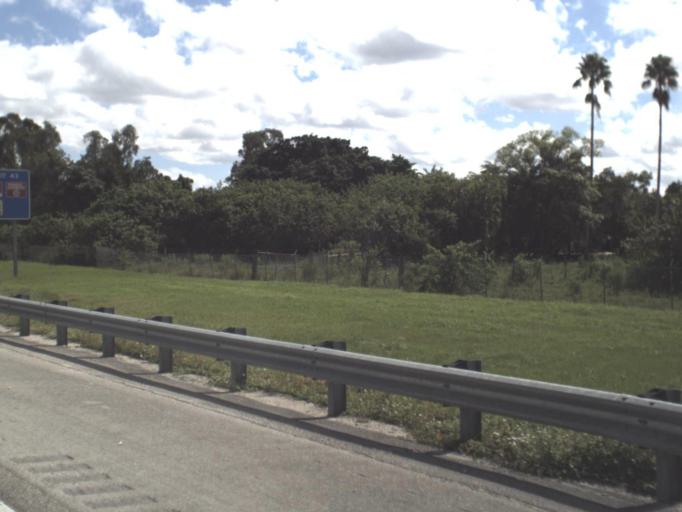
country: US
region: Florida
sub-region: Miami-Dade County
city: Country Club
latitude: 25.9706
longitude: -80.3072
